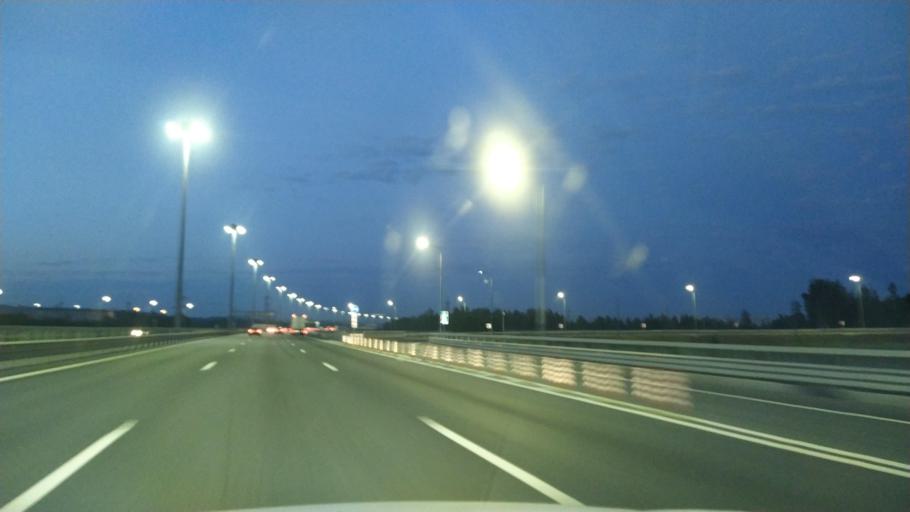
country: RU
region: St.-Petersburg
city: Pargolovo
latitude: 60.0983
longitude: 30.2705
